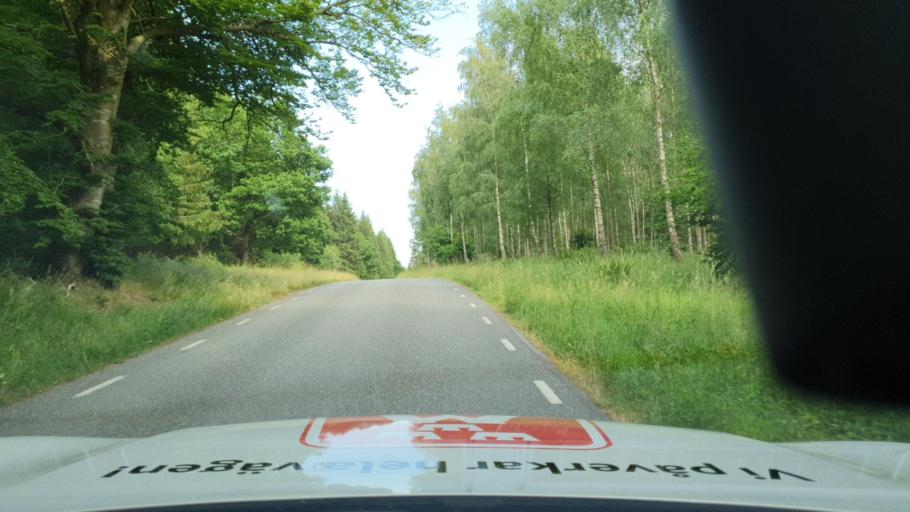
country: SE
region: Skane
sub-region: Kristianstads Kommun
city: Degeberga
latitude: 55.6927
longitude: 14.0724
